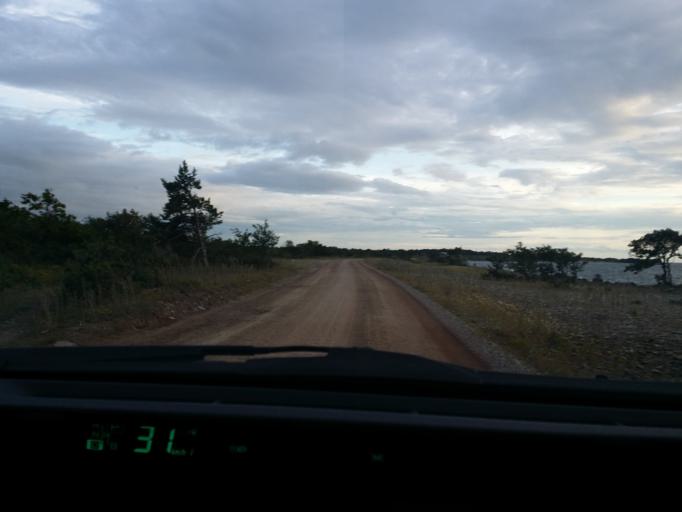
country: SE
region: Kalmar
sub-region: Borgholms Kommun
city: Borgholm
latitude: 57.2118
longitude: 16.9395
